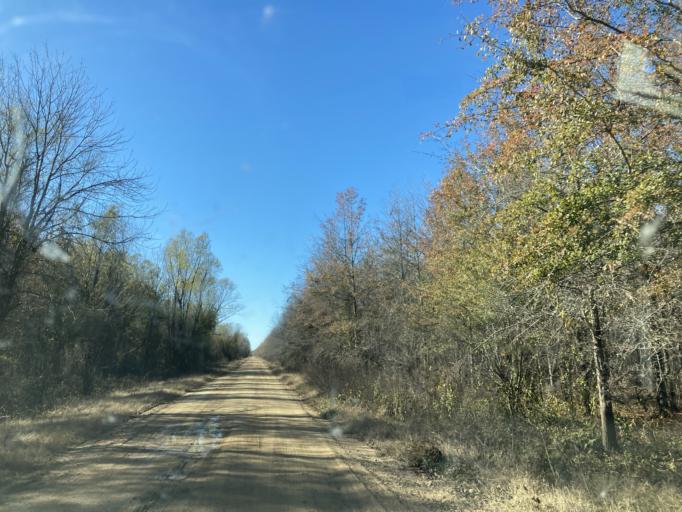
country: US
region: Mississippi
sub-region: Sharkey County
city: Rolling Fork
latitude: 32.7491
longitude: -90.6660
